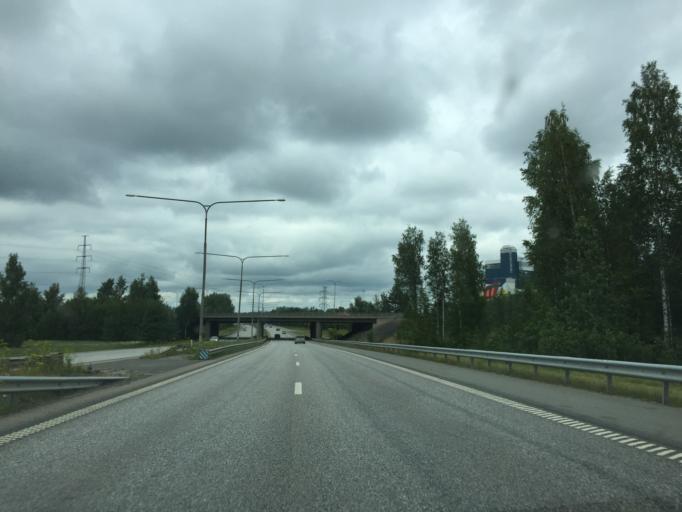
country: SE
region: OErebro
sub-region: Orebro Kommun
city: Orebro
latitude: 59.2624
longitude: 15.1707
